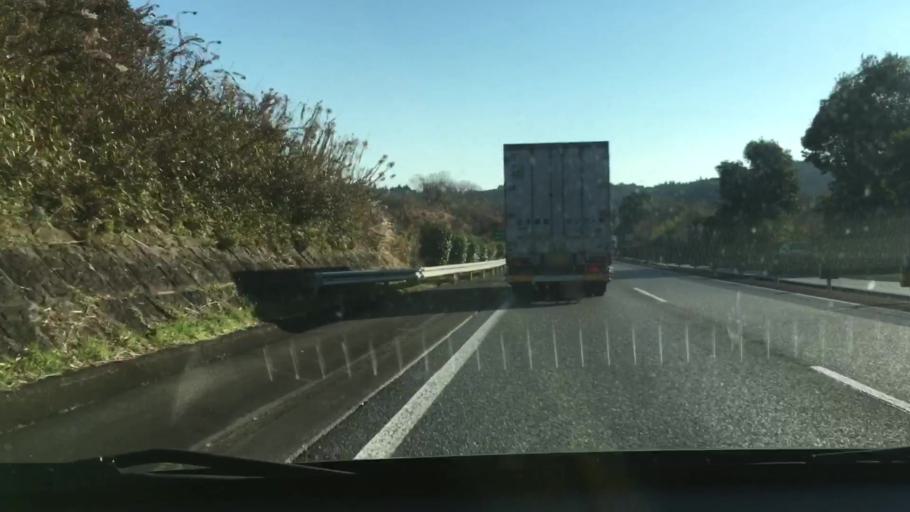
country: JP
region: Kagoshima
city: Kajiki
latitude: 31.8819
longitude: 130.6954
